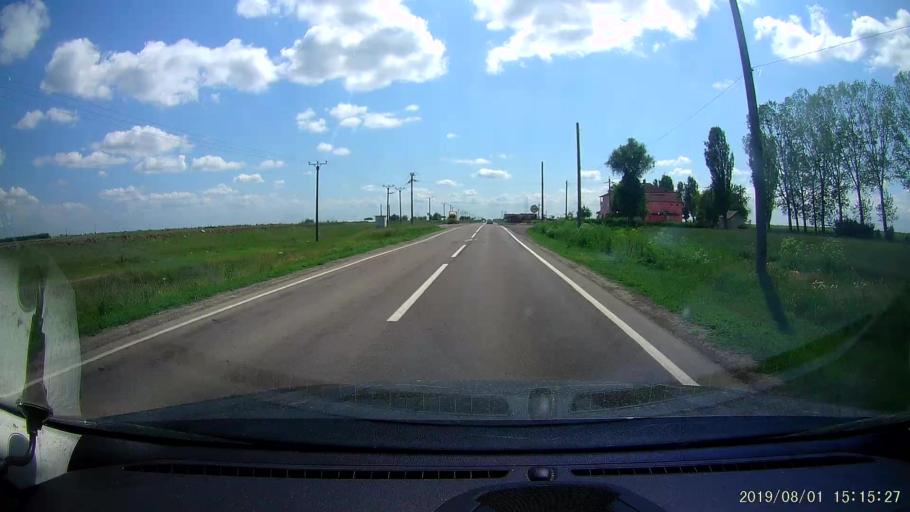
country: RO
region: Braila
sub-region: Comuna Tichilesti
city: Tichilesti
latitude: 45.1639
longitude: 27.8679
